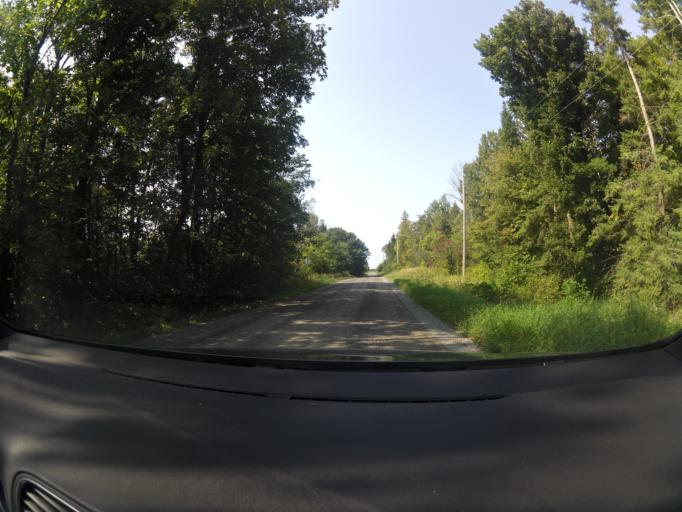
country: CA
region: Ontario
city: Carleton Place
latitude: 45.3447
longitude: -76.1292
